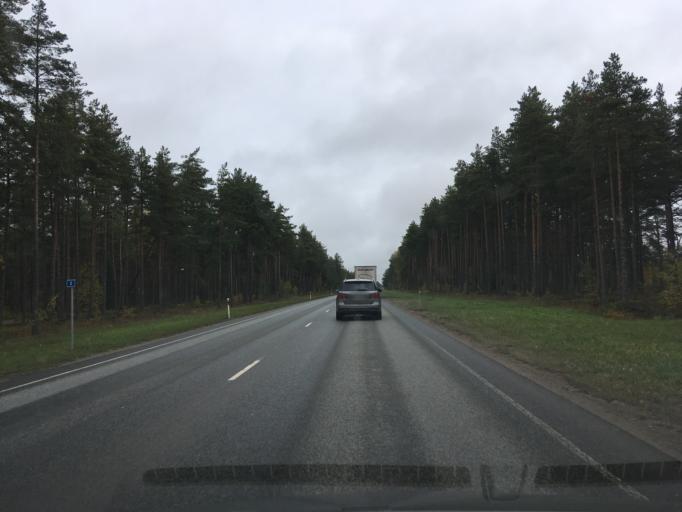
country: EE
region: Harju
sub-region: Saku vald
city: Saku
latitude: 59.3199
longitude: 24.6875
